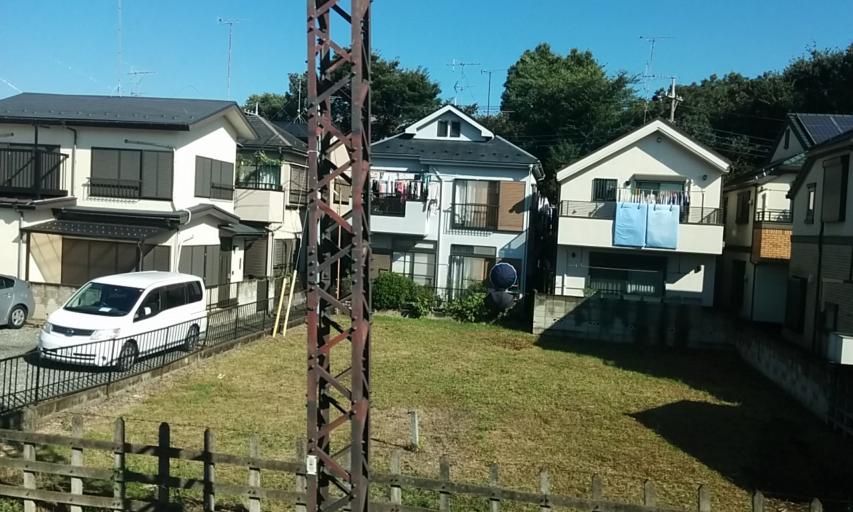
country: JP
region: Tokyo
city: Higashimurayama-shi
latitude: 35.7397
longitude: 139.4787
